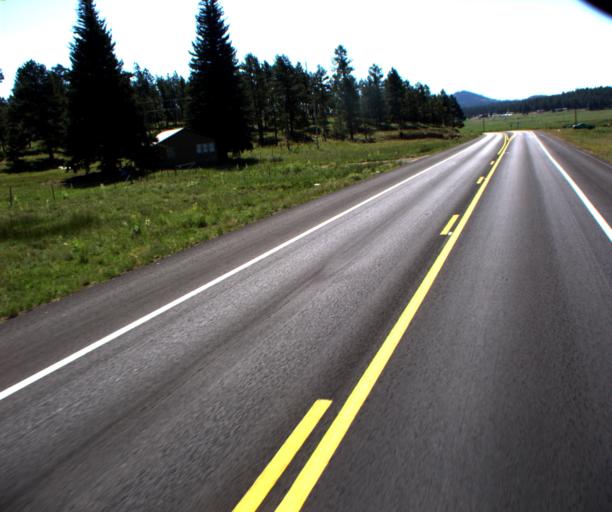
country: US
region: Arizona
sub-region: Apache County
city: Eagar
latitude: 33.8395
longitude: -109.1275
